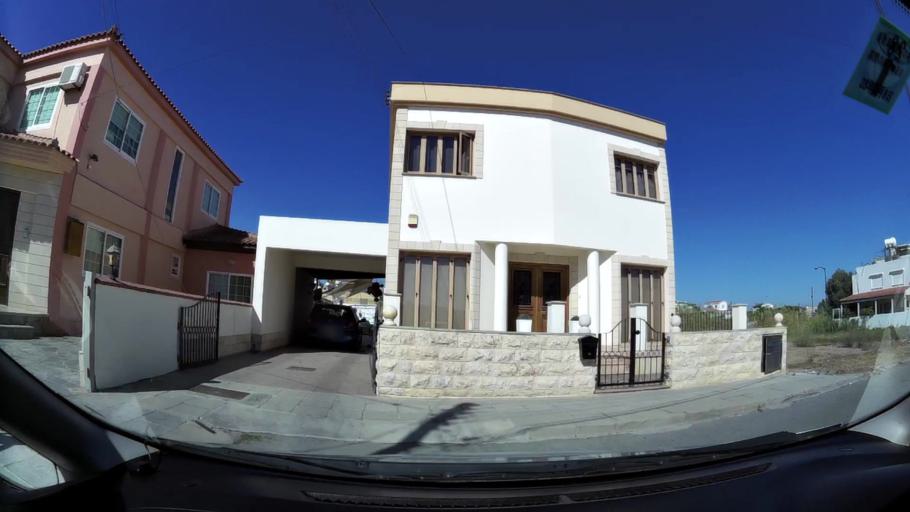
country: CY
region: Larnaka
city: Larnaca
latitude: 34.9331
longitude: 33.6308
